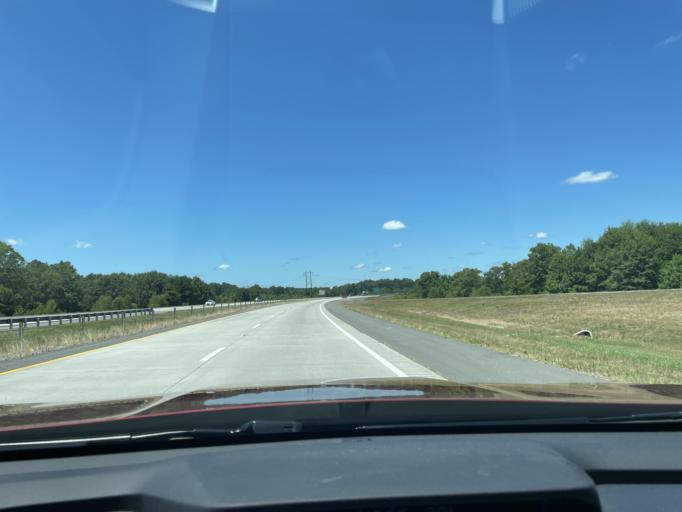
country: US
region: Arkansas
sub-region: Jefferson County
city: Pine Bluff
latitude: 34.1734
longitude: -91.9925
